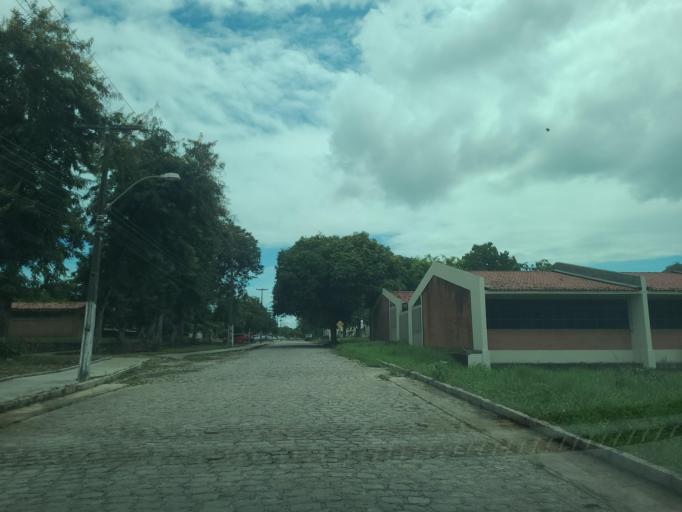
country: BR
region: Alagoas
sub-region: Satuba
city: Satuba
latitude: -9.5557
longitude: -35.7751
